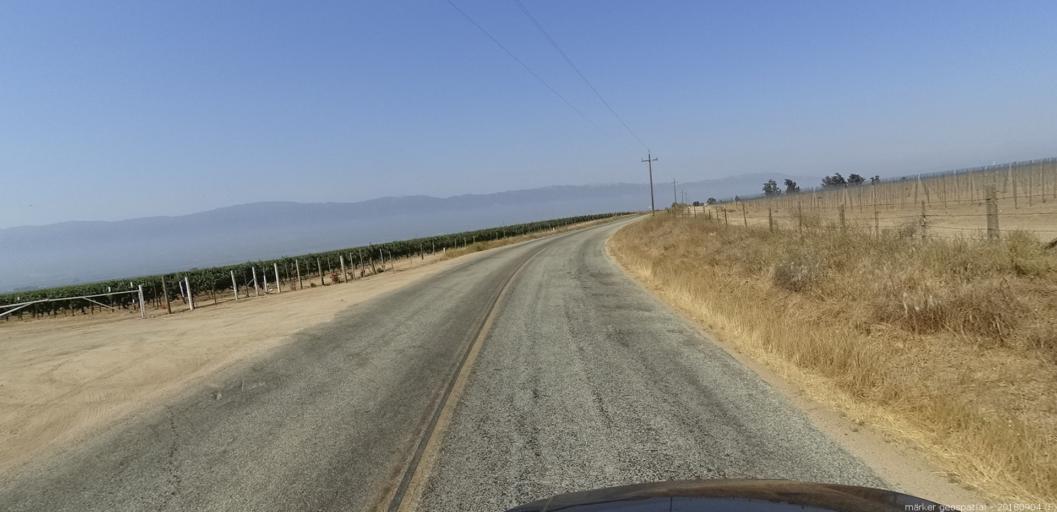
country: US
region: California
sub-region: Monterey County
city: Gonzales
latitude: 36.5039
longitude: -121.3740
